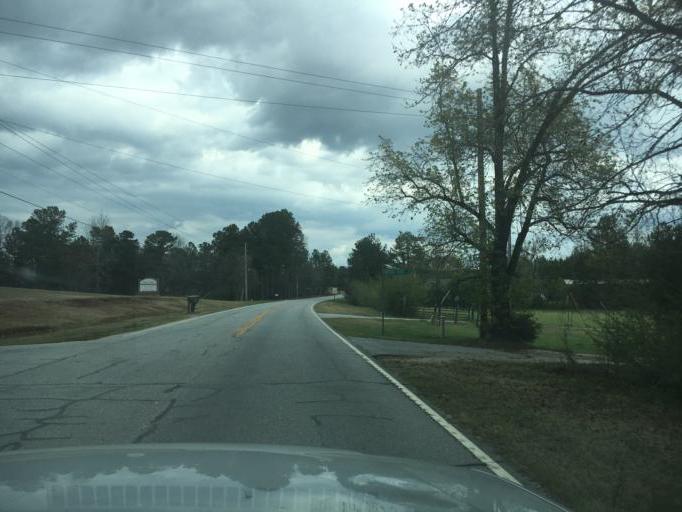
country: US
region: South Carolina
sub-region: Oconee County
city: Walhalla
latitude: 34.7119
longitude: -83.0703
